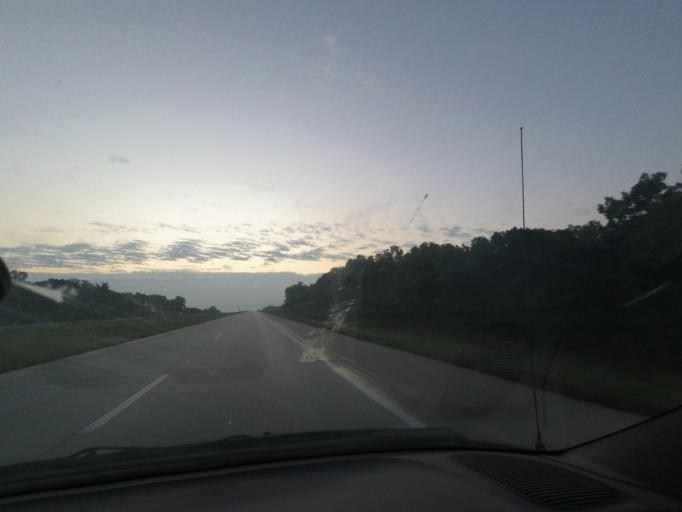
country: US
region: Missouri
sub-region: Linn County
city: Marceline
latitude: 39.7591
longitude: -92.8327
